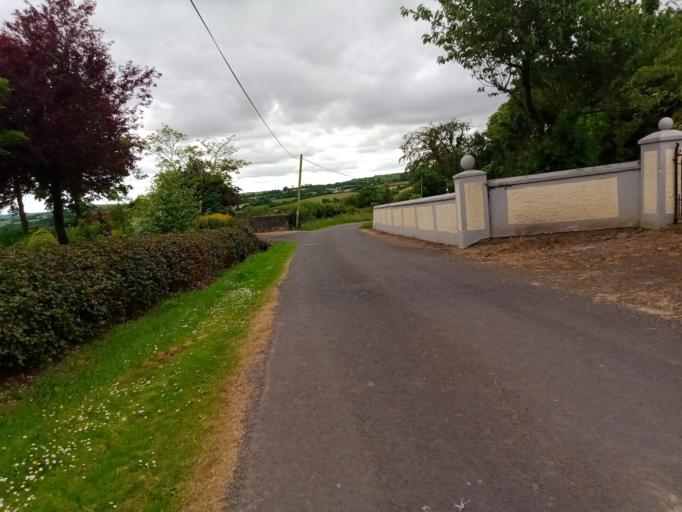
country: IE
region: Leinster
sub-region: Kilkenny
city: Ballyragget
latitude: 52.7727
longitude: -7.4673
